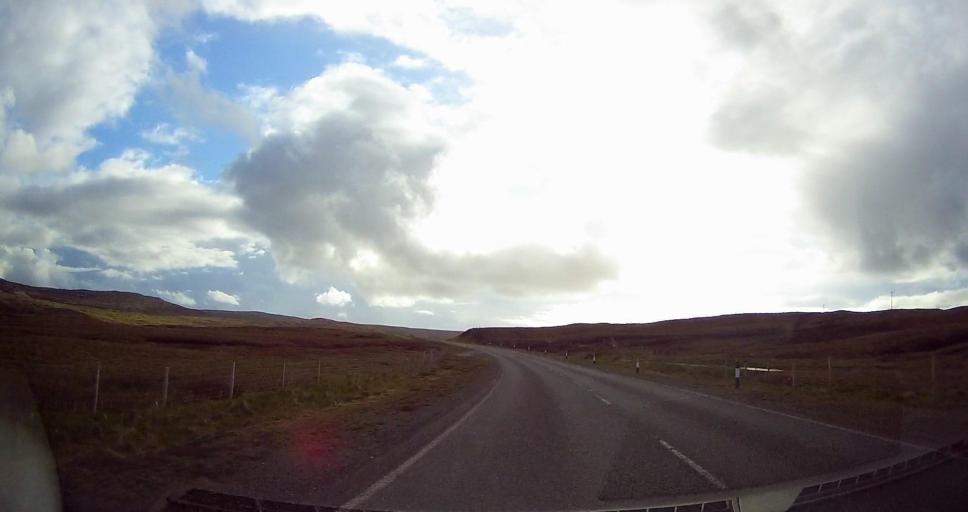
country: GB
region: Scotland
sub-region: Shetland Islands
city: Lerwick
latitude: 60.3494
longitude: -1.2168
